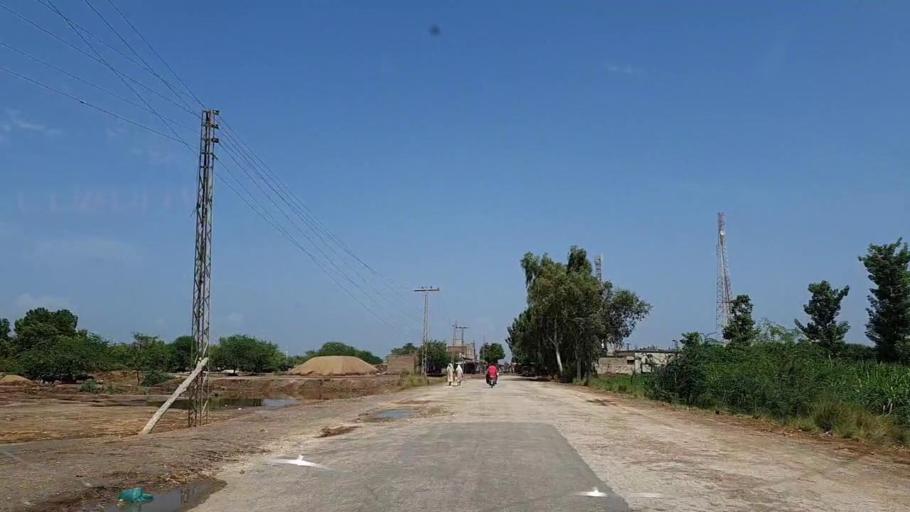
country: PK
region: Sindh
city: Naushahro Firoz
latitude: 26.8115
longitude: 68.1946
